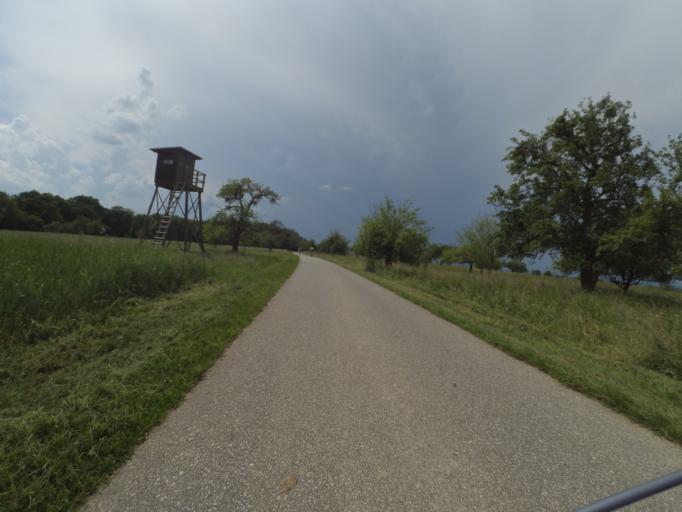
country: DE
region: Rheinland-Pfalz
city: Hatzenport
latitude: 50.2131
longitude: 7.4173
